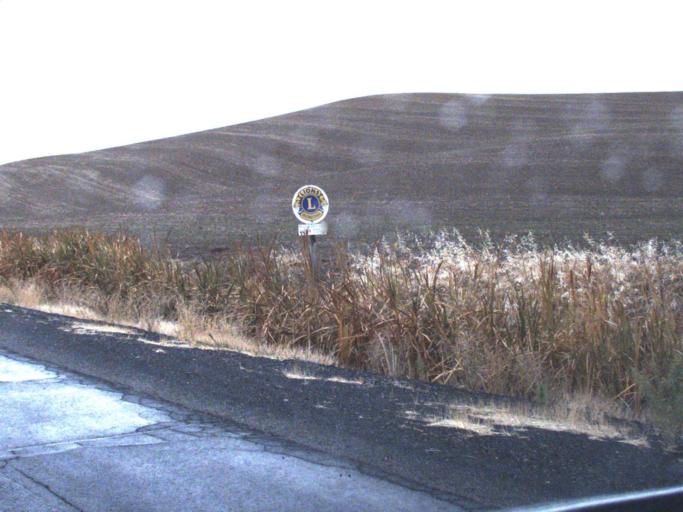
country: US
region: Washington
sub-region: Whitman County
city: Pullman
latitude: 46.7386
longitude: -117.2278
